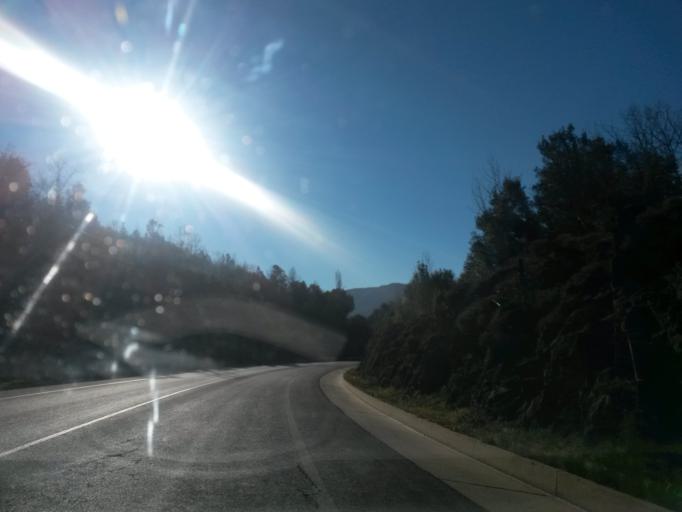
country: ES
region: Catalonia
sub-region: Provincia de Girona
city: Bas
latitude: 42.1129
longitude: 2.4899
